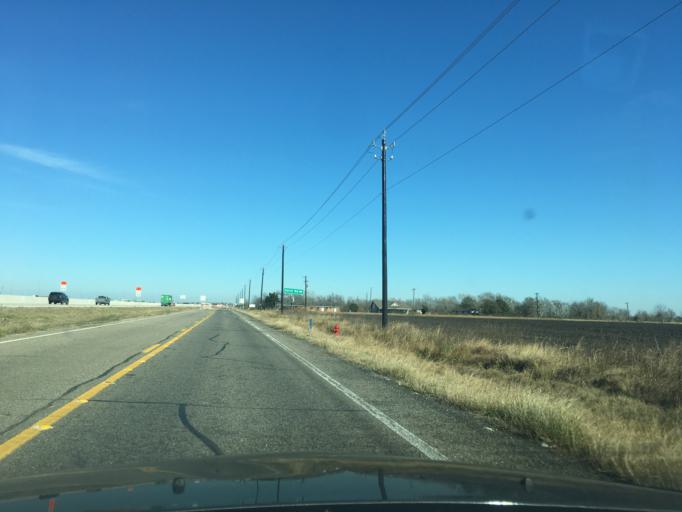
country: US
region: Texas
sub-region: Wharton County
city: East Bernard
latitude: 29.4550
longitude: -95.9842
